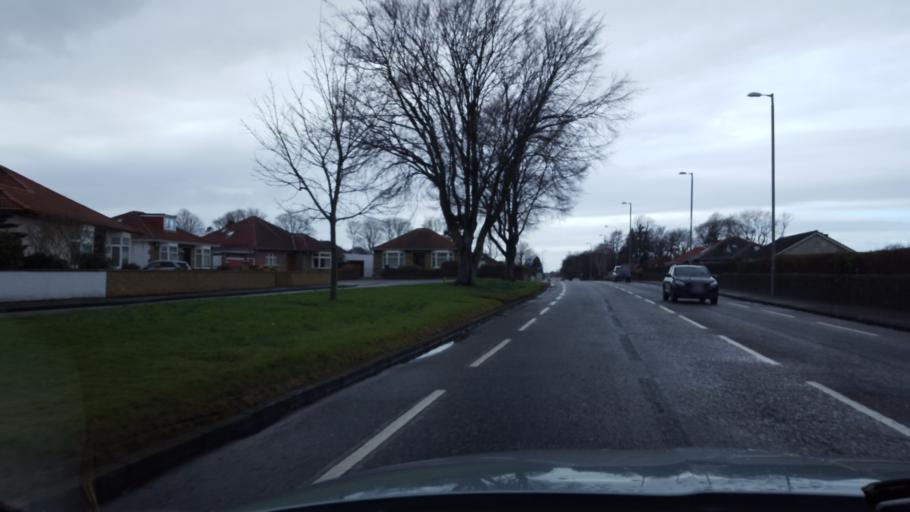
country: GB
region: Scotland
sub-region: South Ayrshire
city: Prestwick
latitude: 55.4557
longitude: -4.6028
